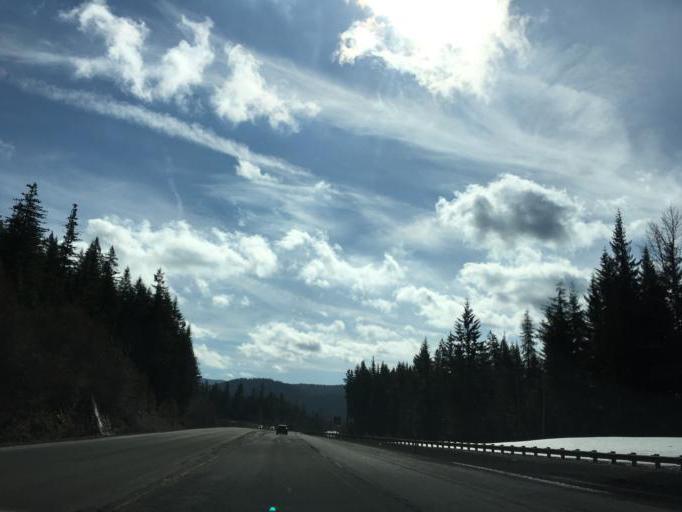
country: US
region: Oregon
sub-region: Clackamas County
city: Mount Hood Village
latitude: 45.2887
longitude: -121.7331
